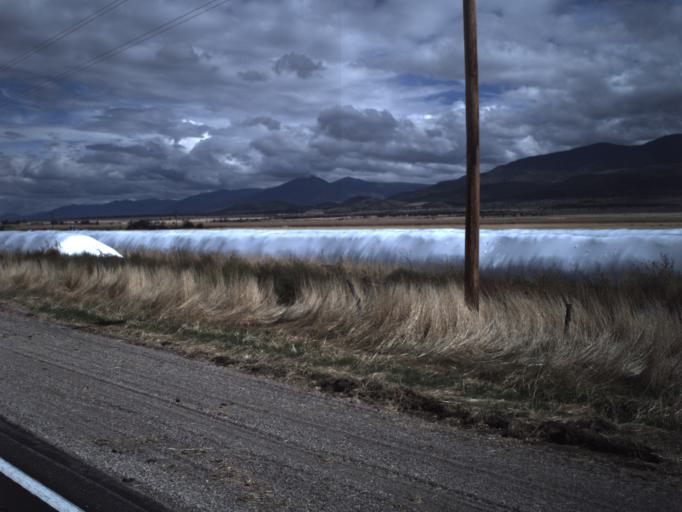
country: US
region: Utah
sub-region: Millard County
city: Fillmore
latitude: 38.8559
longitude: -112.4206
